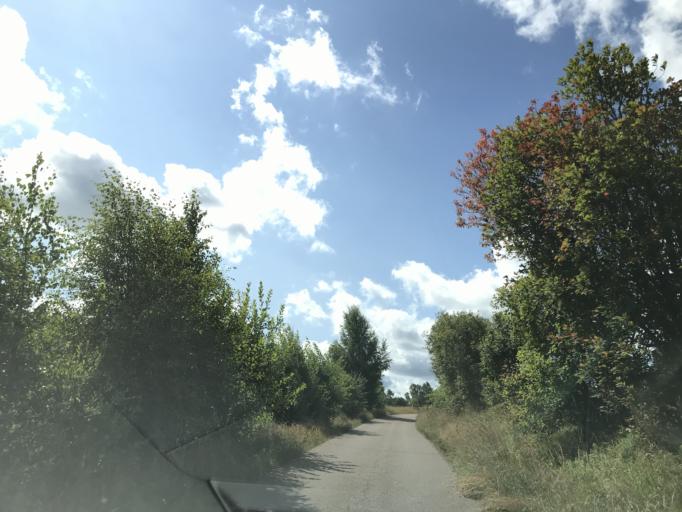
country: SE
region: Halland
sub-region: Laholms Kommun
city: Knared
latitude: 56.5140
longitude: 13.3020
